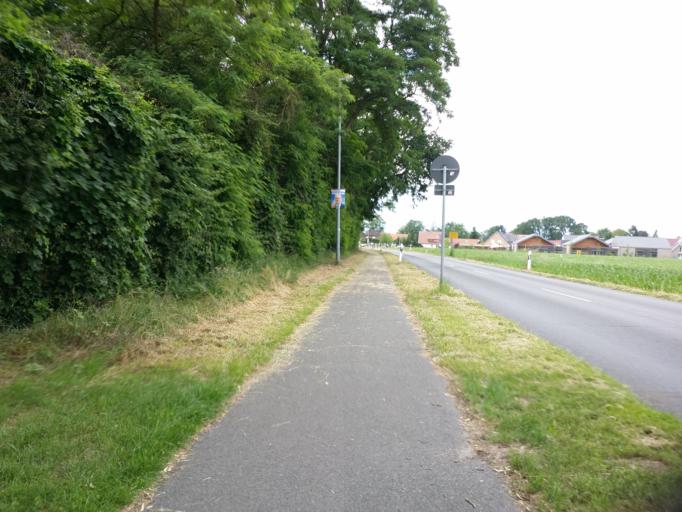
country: DE
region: Lower Saxony
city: Stuhr
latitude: 53.0319
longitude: 8.7101
